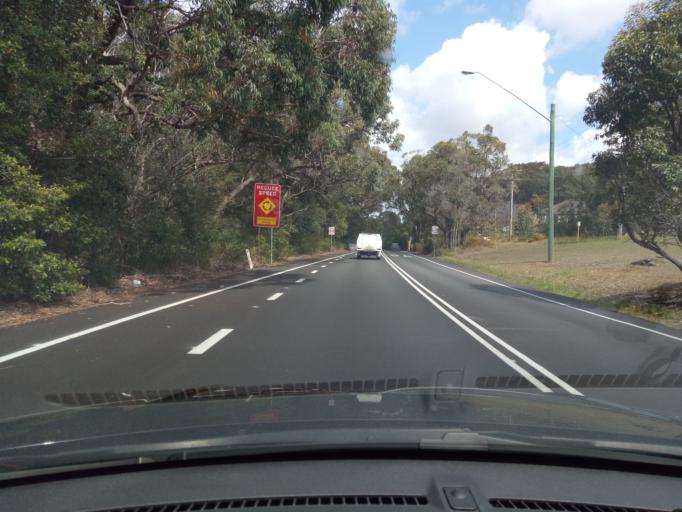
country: AU
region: New South Wales
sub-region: Gosford Shire
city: Forresters Beach
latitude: -33.4136
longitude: 151.4527
